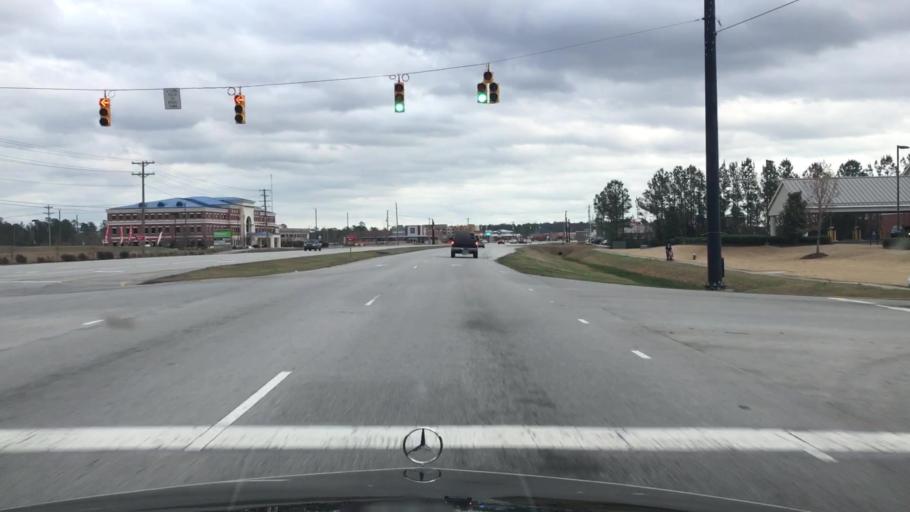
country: US
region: North Carolina
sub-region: Onslow County
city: Pumpkin Center
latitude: 34.8000
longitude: -77.4176
